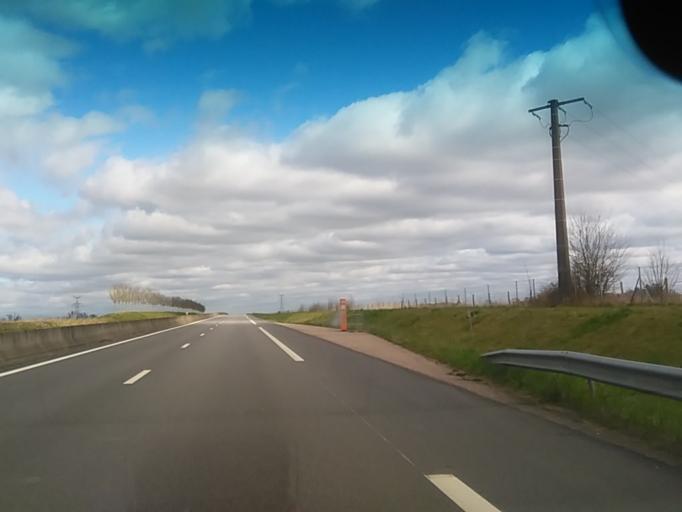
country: FR
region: Haute-Normandie
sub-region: Departement de l'Eure
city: Bourg-Achard
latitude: 49.3023
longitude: 0.7996
